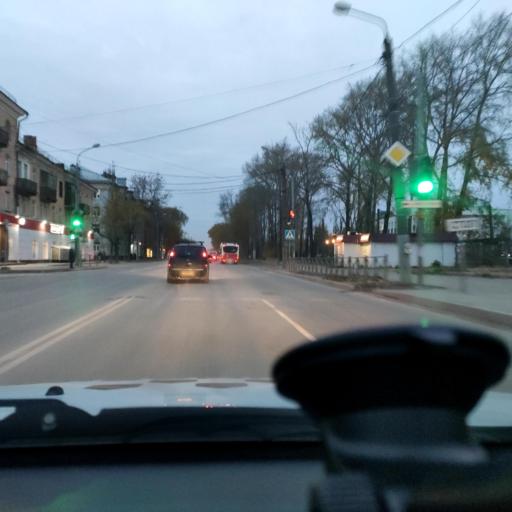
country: RU
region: Perm
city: Froly
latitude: 57.9604
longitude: 56.2434
